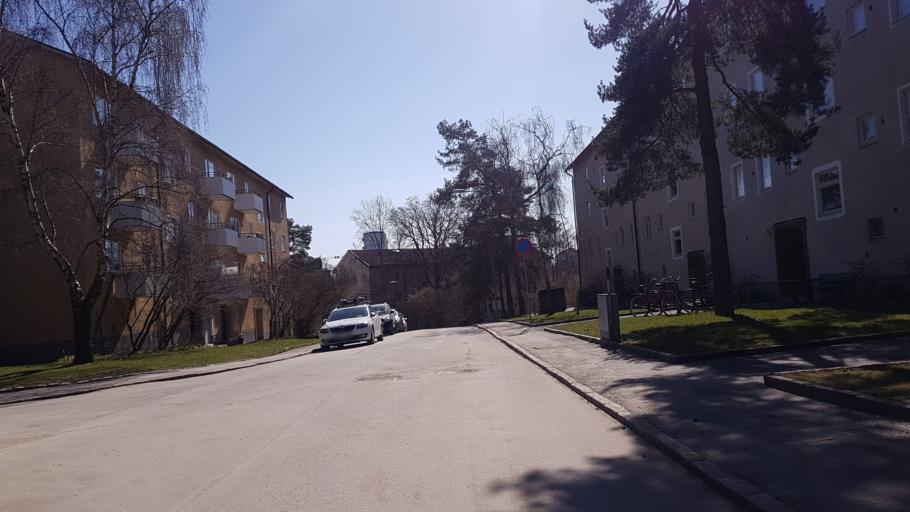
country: SE
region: Stockholm
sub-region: Nacka Kommun
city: Nacka
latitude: 59.2954
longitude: 18.1168
